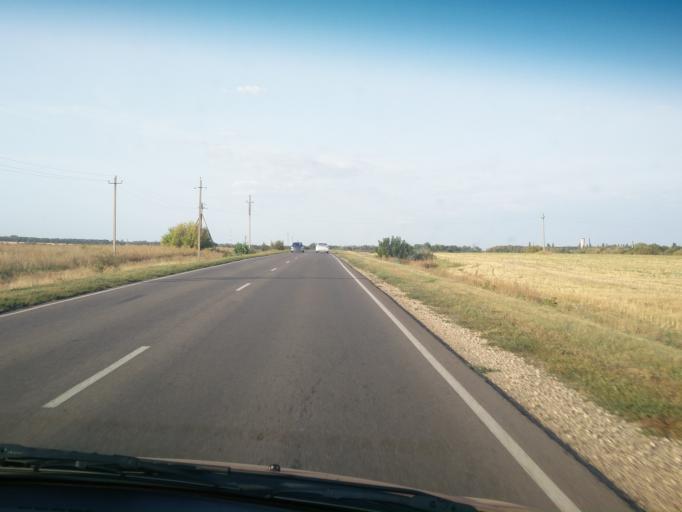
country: RU
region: Voronezj
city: Ramon'
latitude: 51.9316
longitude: 39.3302
